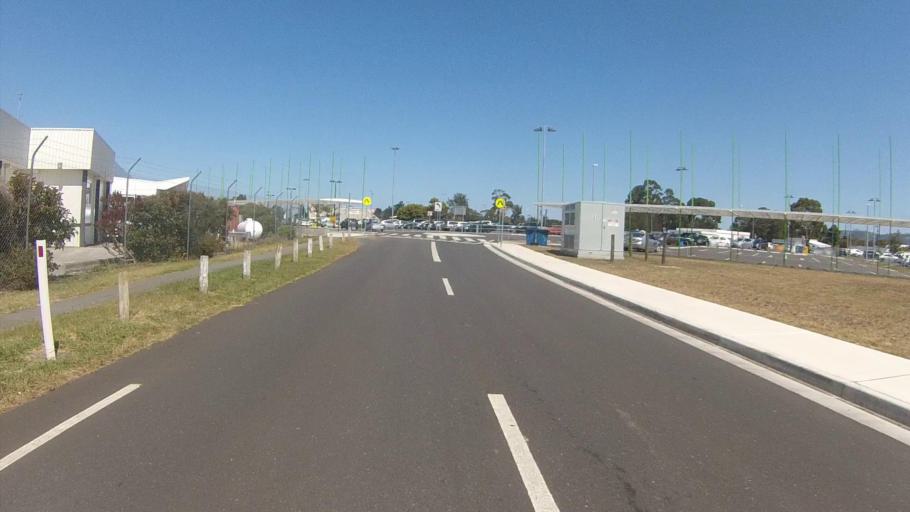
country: AU
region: Tasmania
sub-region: Clarence
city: Seven Mile Beach
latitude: -42.8361
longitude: 147.5036
